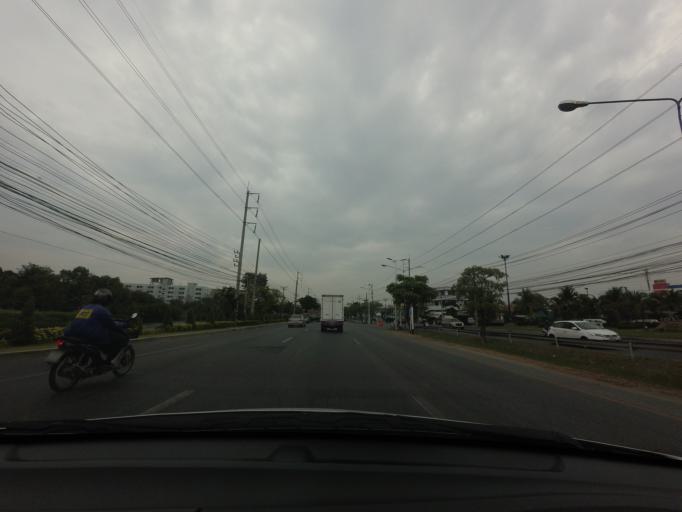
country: TH
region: Samut Prakan
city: Samut Prakan
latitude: 13.5559
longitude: 100.6134
